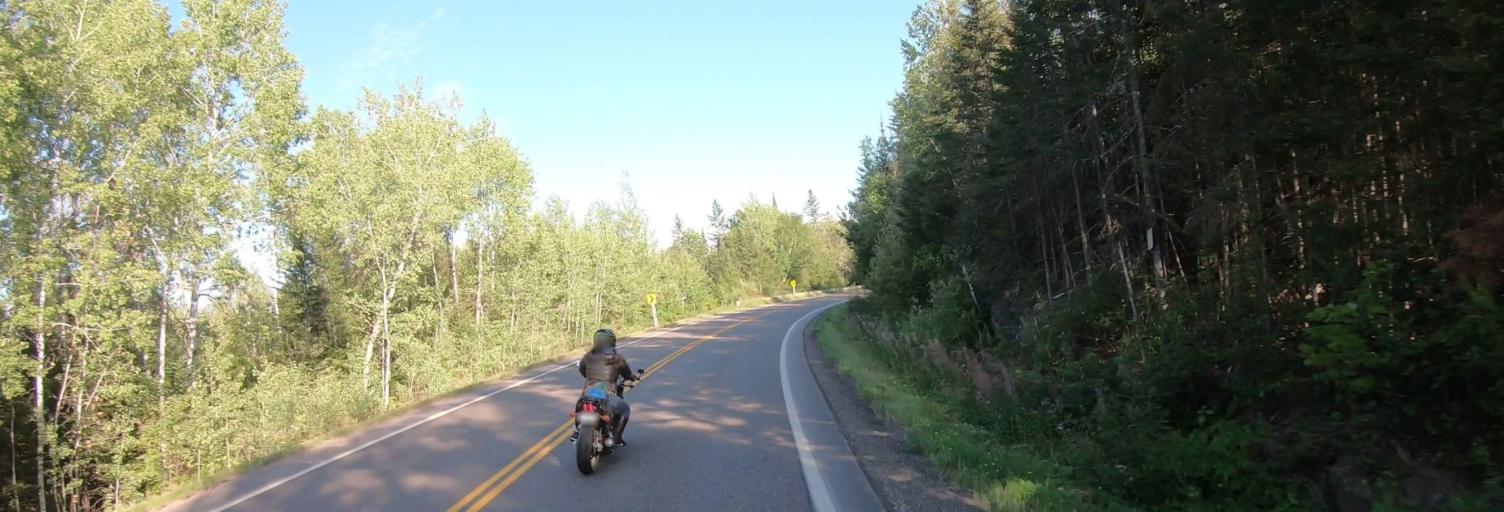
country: US
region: Minnesota
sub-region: Saint Louis County
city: Ely
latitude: 47.9616
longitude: -91.5585
